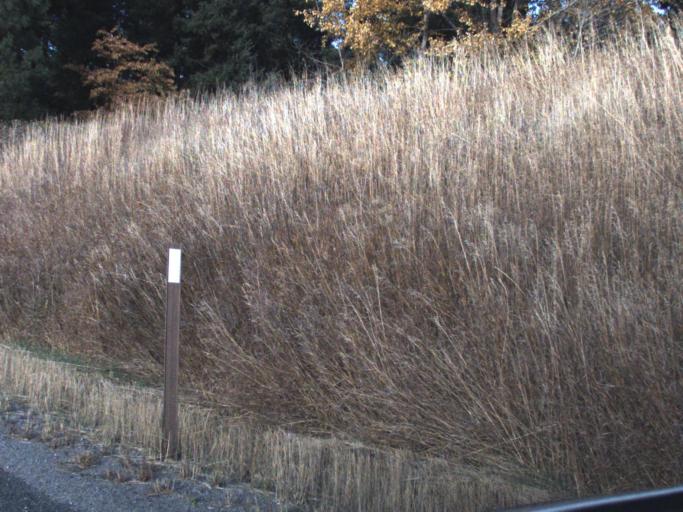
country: US
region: Washington
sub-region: Stevens County
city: Kettle Falls
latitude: 48.4504
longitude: -118.1722
